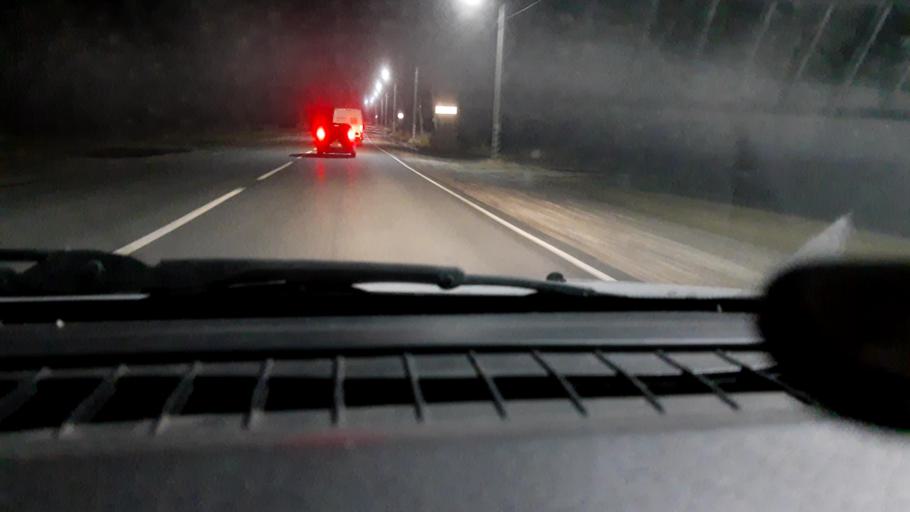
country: RU
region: Nizjnij Novgorod
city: Linda
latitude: 56.5713
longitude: 44.0239
